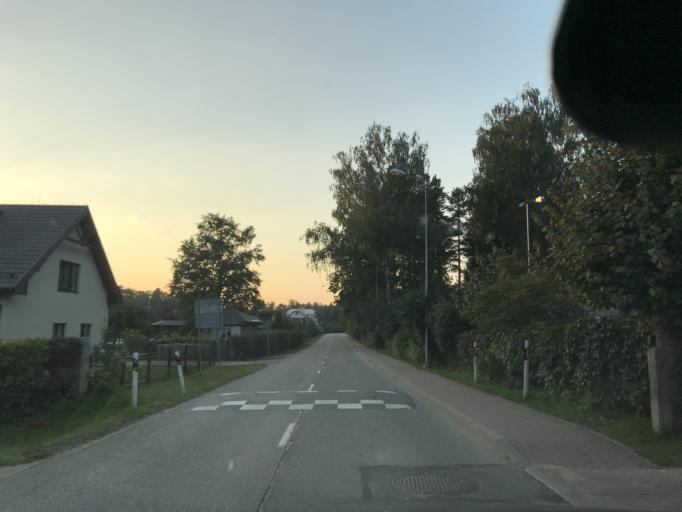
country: LV
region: Ikskile
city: Ikskile
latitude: 56.8346
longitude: 24.4910
